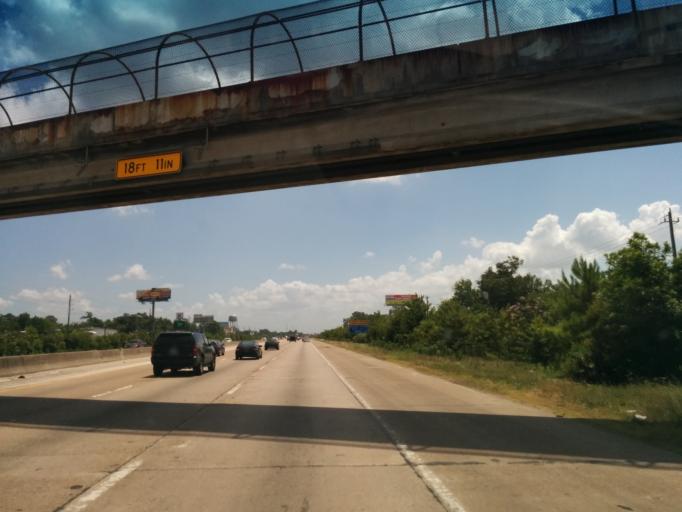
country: US
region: Texas
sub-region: Harris County
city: Channelview
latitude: 29.7810
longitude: -95.1165
